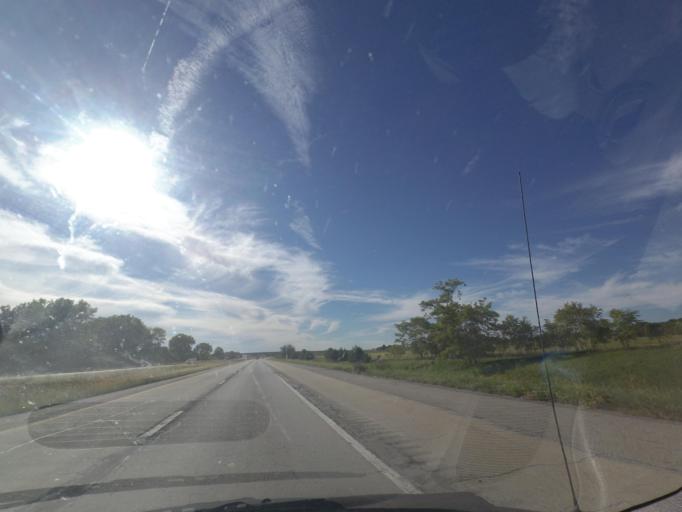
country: US
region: Illinois
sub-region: Macon County
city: Forsyth
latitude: 39.9079
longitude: -88.9692
